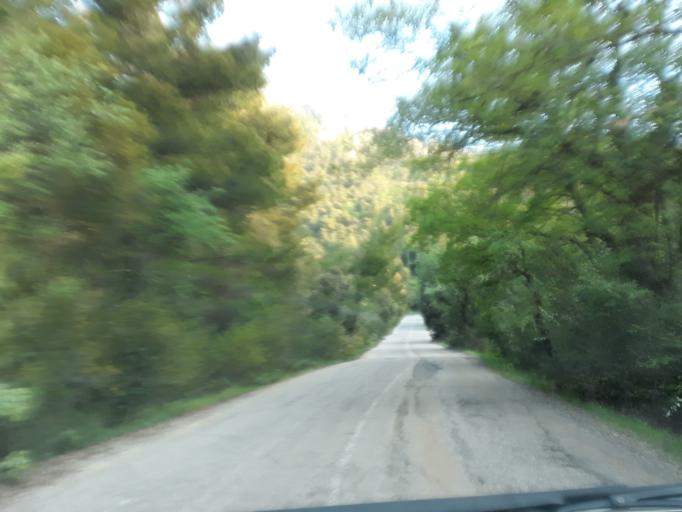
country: GR
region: Attica
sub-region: Nomarchia Anatolikis Attikis
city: Afidnes
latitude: 38.1917
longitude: 23.7835
